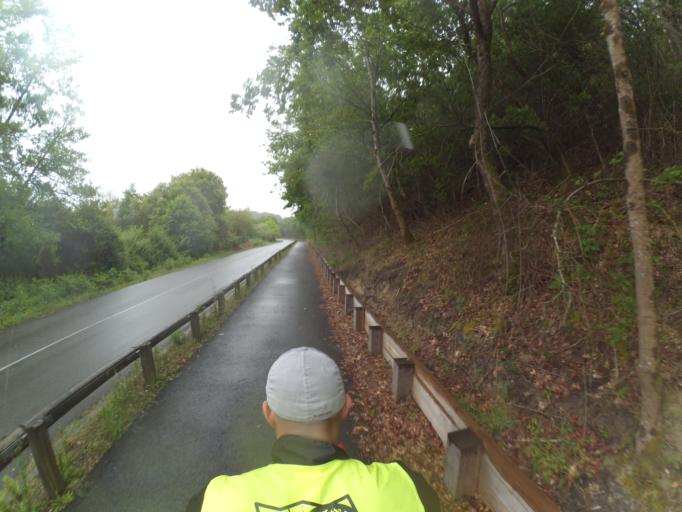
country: FR
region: Aquitaine
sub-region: Departement des Landes
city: Mimizan
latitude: 44.2327
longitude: -1.2235
